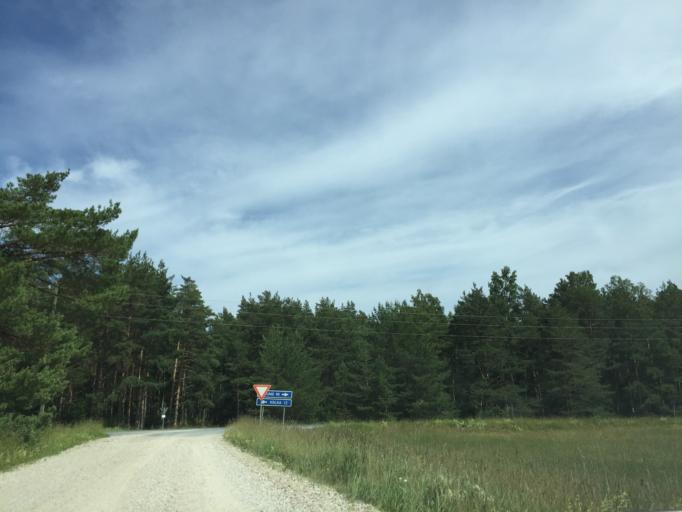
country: LV
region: Dundaga
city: Dundaga
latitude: 57.6266
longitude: 22.5760
